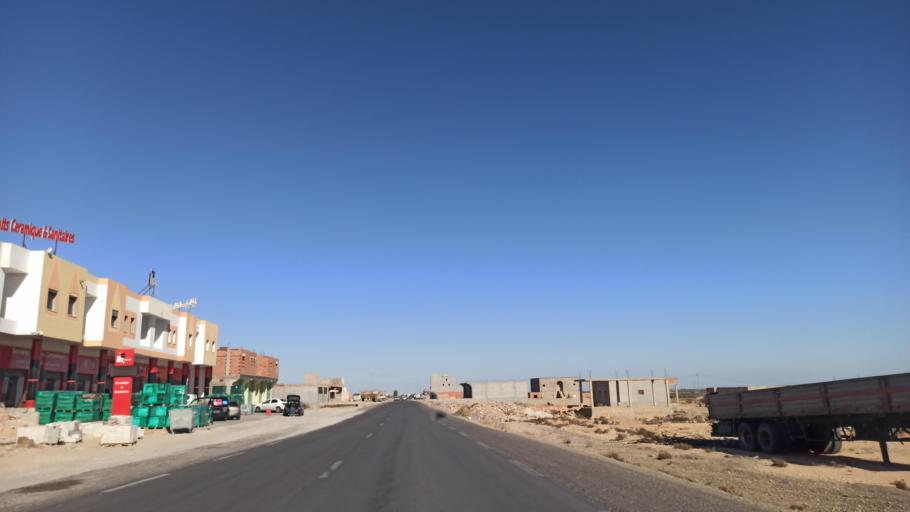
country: TN
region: Sidi Bu Zayd
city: Bi'r al Hufayy
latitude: 34.9461
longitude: 9.2079
